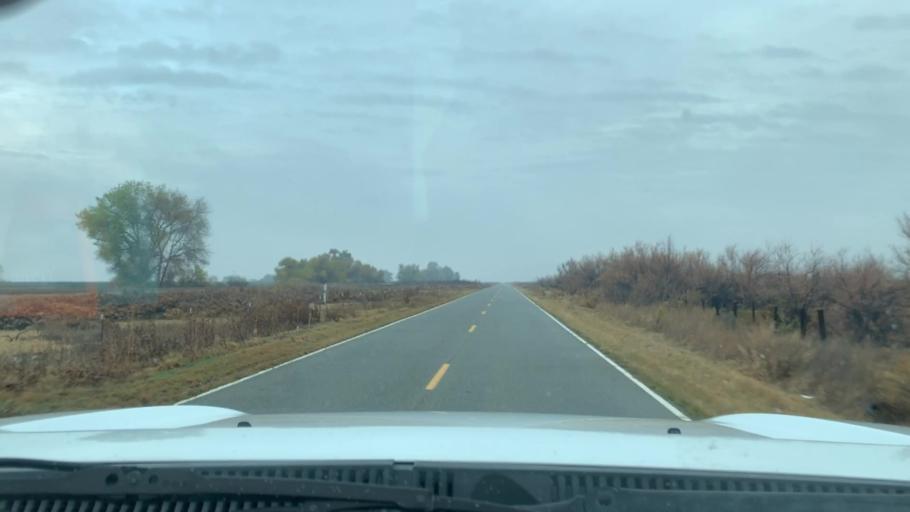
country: US
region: California
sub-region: Kern County
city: Lost Hills
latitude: 35.7272
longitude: -119.5794
